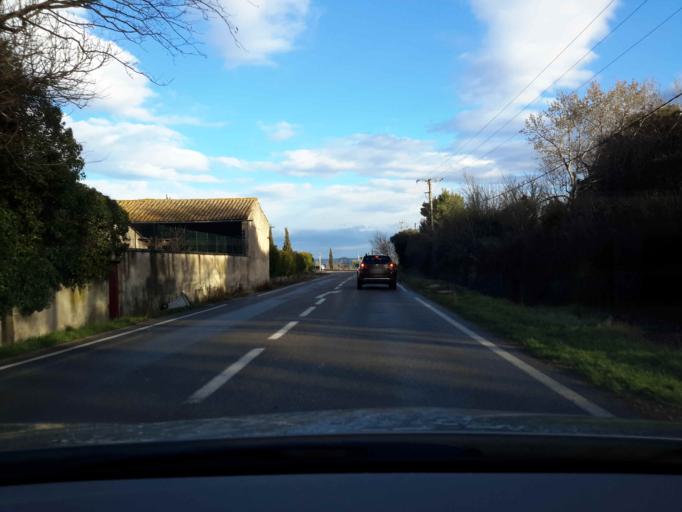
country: FR
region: Languedoc-Roussillon
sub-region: Departement du Gard
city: Generac
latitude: 43.7438
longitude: 4.3423
